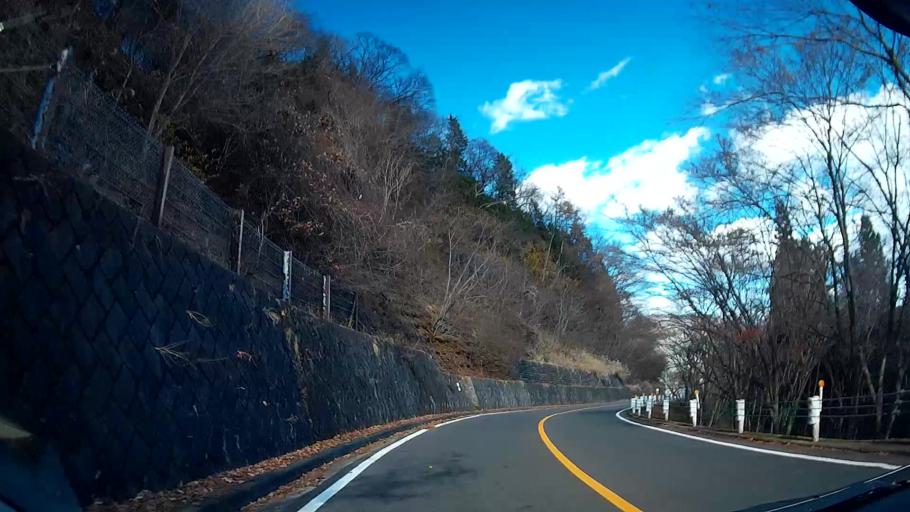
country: JP
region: Yamanashi
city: Uenohara
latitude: 35.7630
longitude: 139.0383
